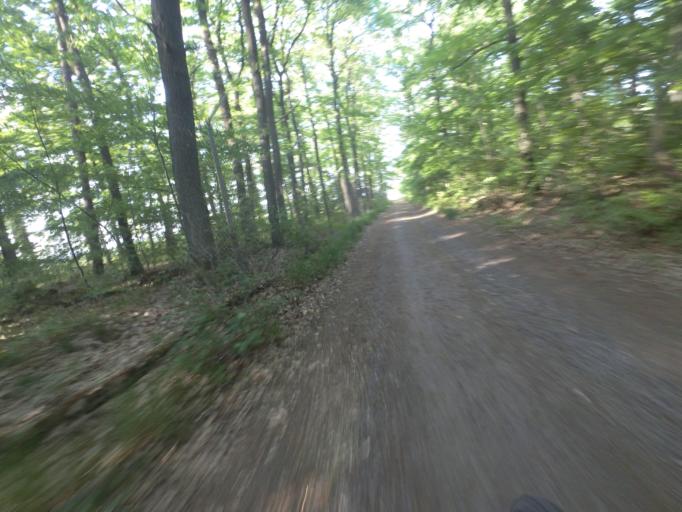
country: DE
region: Rheinland-Pfalz
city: Kirchheimbolanden
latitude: 49.6646
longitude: 7.9827
